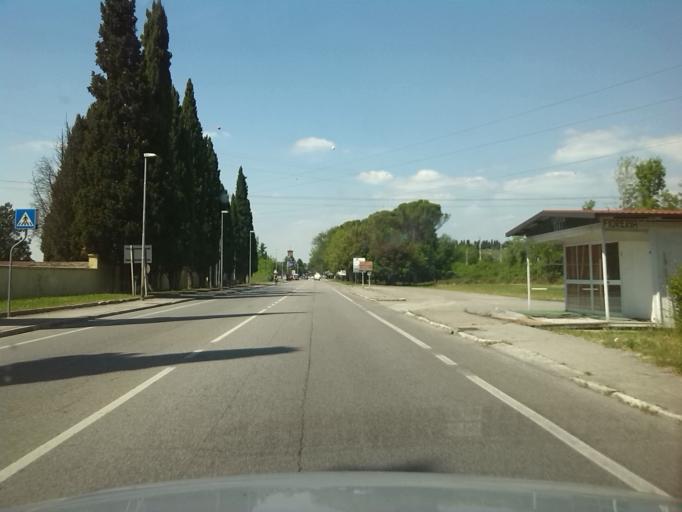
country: IT
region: Friuli Venezia Giulia
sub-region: Provincia di Gorizia
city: Fogliano
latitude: 45.8593
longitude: 13.4838
